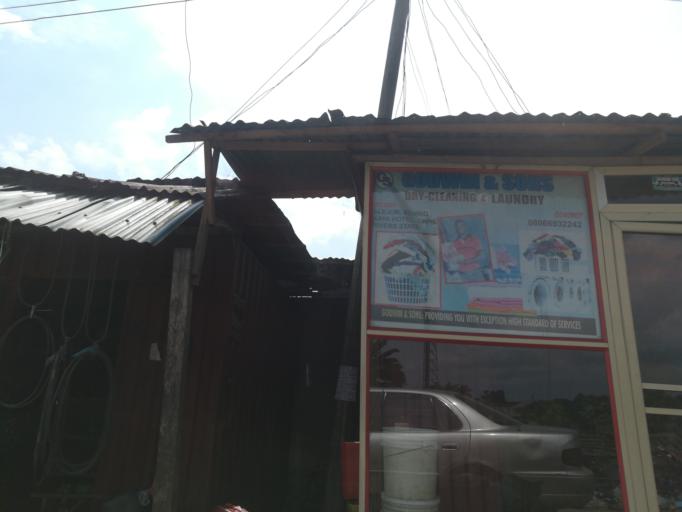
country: NG
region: Rivers
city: Okrika
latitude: 4.7271
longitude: 7.1554
